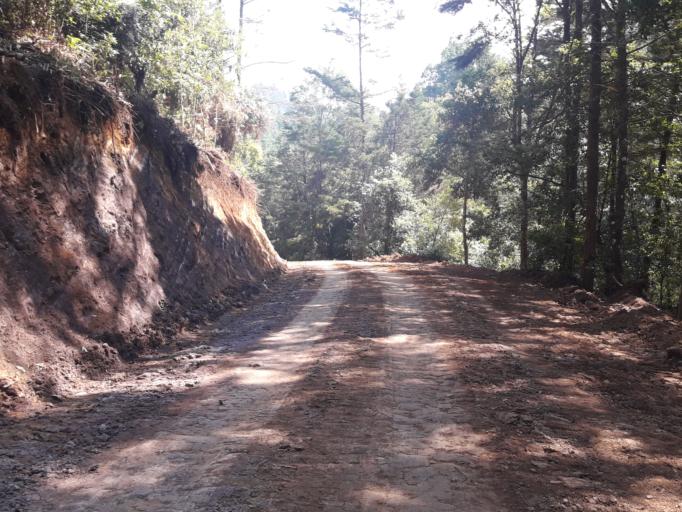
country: GT
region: Quiche
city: Nebaj
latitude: 15.4257
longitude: -91.1367
